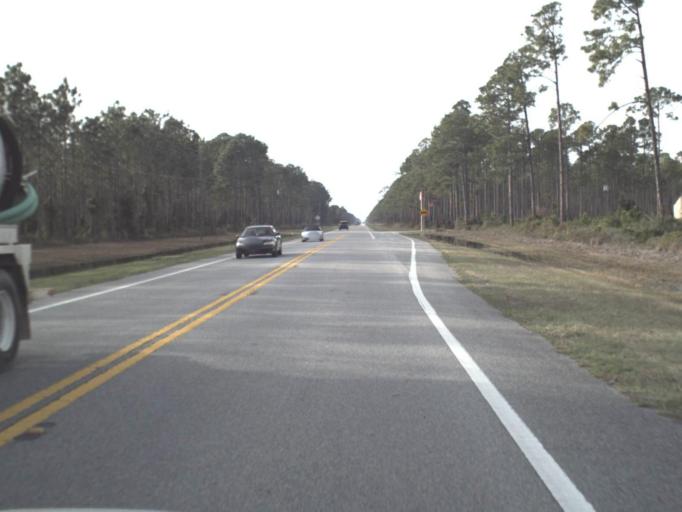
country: US
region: Florida
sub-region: Bay County
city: Mexico Beach
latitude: 29.9978
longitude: -85.4966
